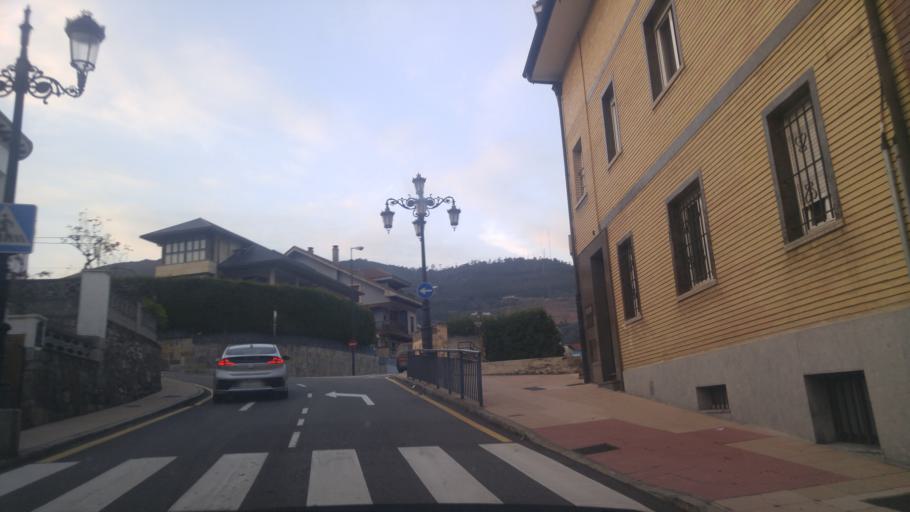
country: ES
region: Asturias
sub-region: Province of Asturias
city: Oviedo
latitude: 43.3710
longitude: -5.8578
